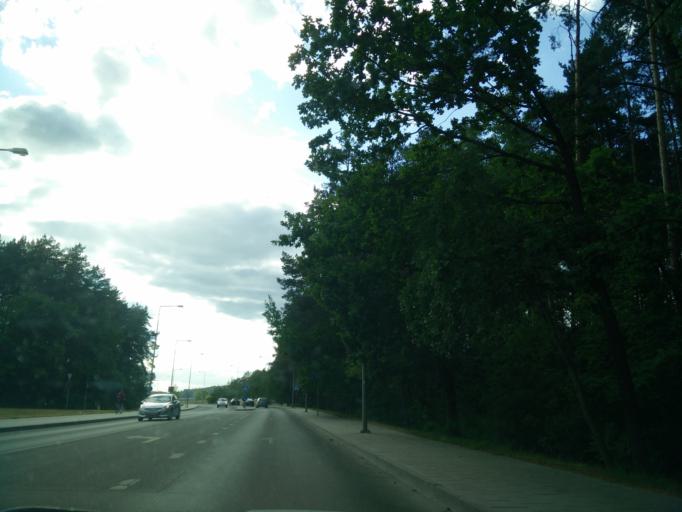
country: LT
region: Vilnius County
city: Lazdynai
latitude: 54.6695
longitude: 25.2114
